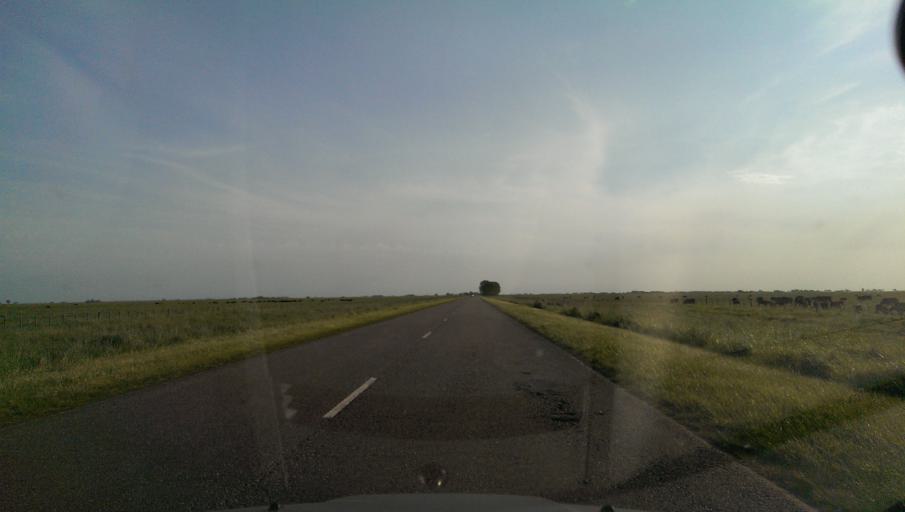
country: AR
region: Buenos Aires
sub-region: Partido de General La Madrid
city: General La Madrid
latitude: -37.5090
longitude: -61.2224
